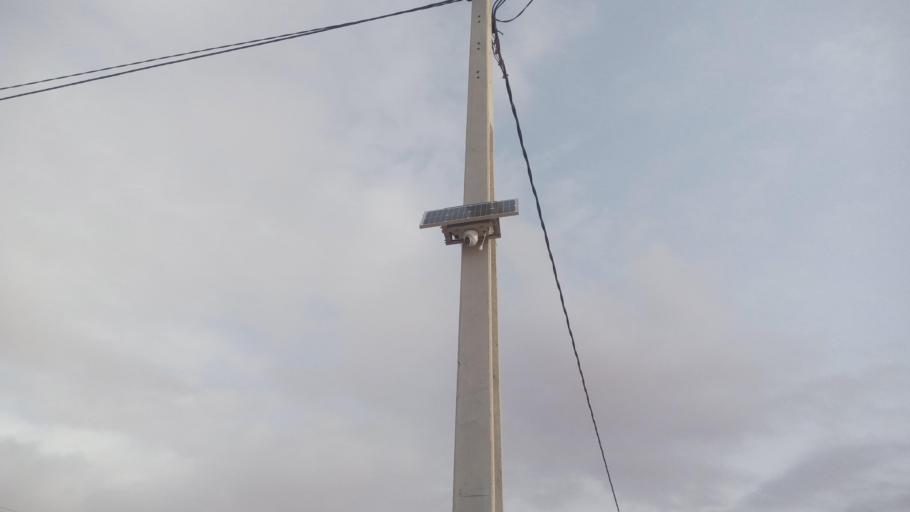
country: TN
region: Tataouine
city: Tataouine
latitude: 33.0568
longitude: 10.6554
